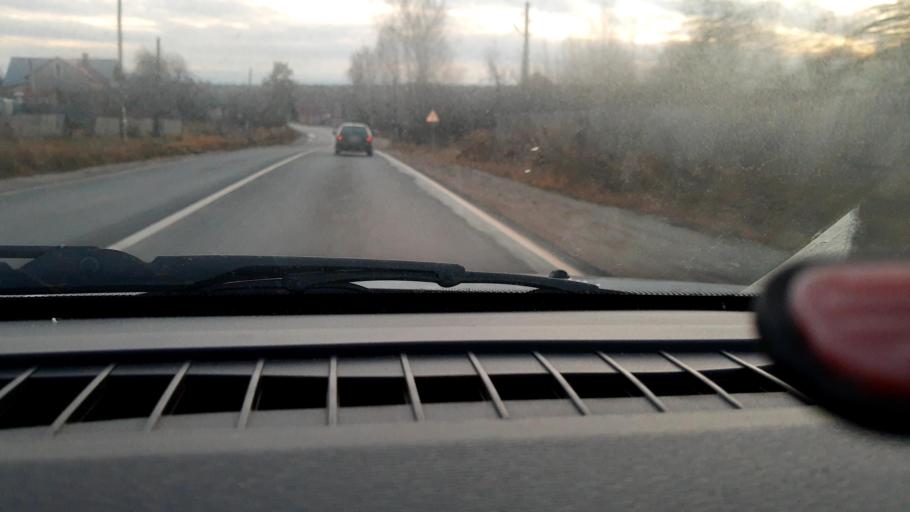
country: RU
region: Nizjnij Novgorod
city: Krasnyye Baki
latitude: 57.0698
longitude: 45.1388
